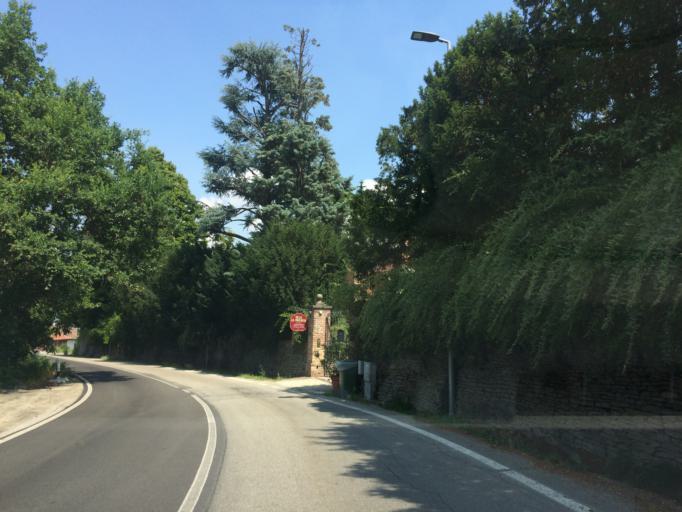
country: IT
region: Piedmont
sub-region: Provincia di Cuneo
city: Alba
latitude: 44.6977
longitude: 8.0473
